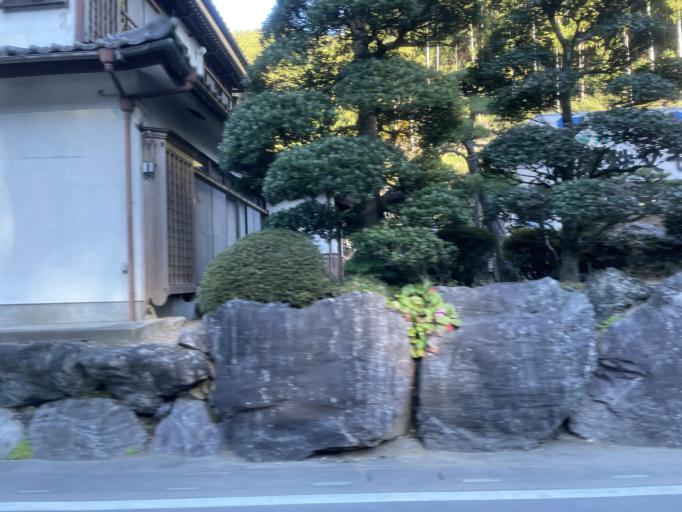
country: JP
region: Saitama
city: Yorii
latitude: 36.0634
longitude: 139.1862
